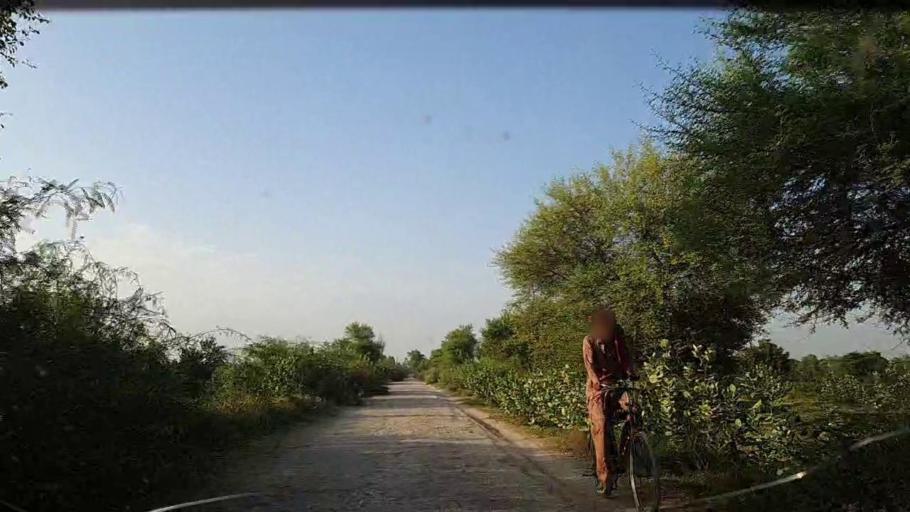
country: PK
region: Sindh
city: Pano Aqil
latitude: 27.9169
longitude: 69.2008
